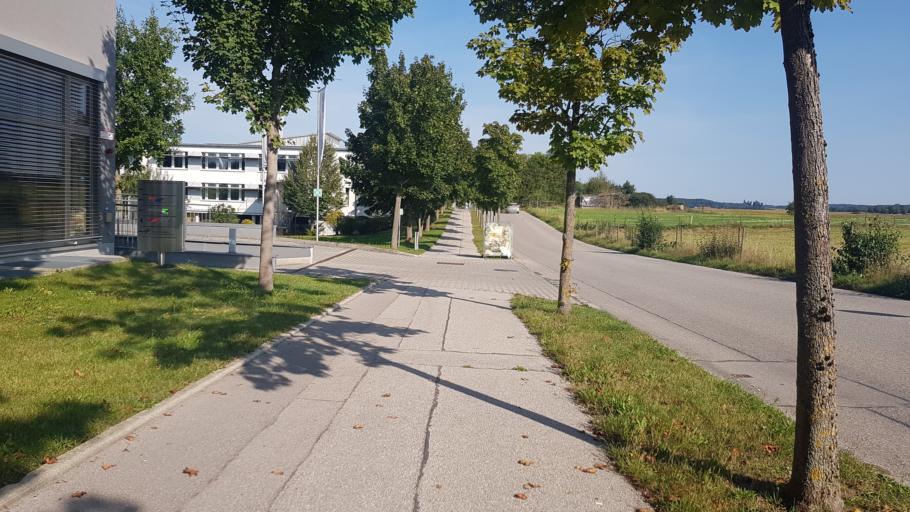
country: DE
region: Bavaria
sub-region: Upper Bavaria
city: Wessling
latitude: 48.0806
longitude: 11.2668
